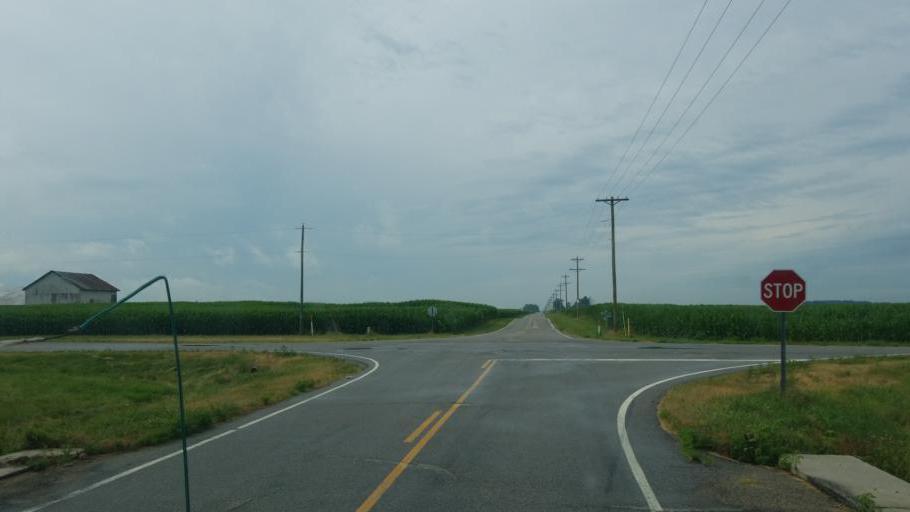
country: US
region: Ohio
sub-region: Defiance County
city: Hicksville
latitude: 41.3254
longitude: -84.6899
